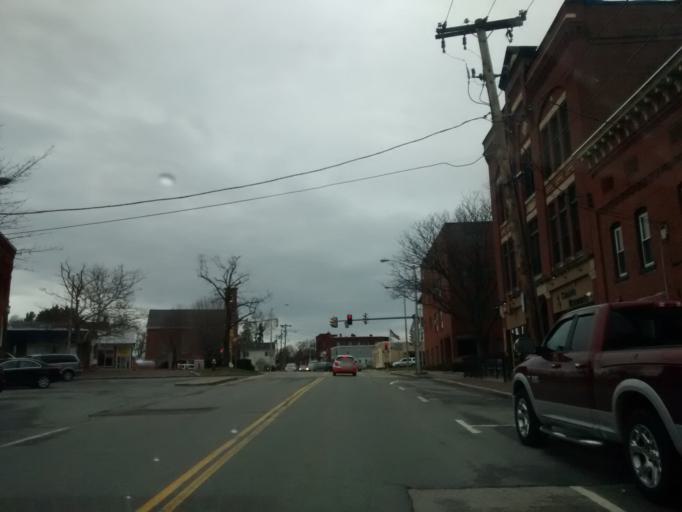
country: US
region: Massachusetts
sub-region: Worcester County
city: Millbury
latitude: 42.1906
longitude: -71.7604
